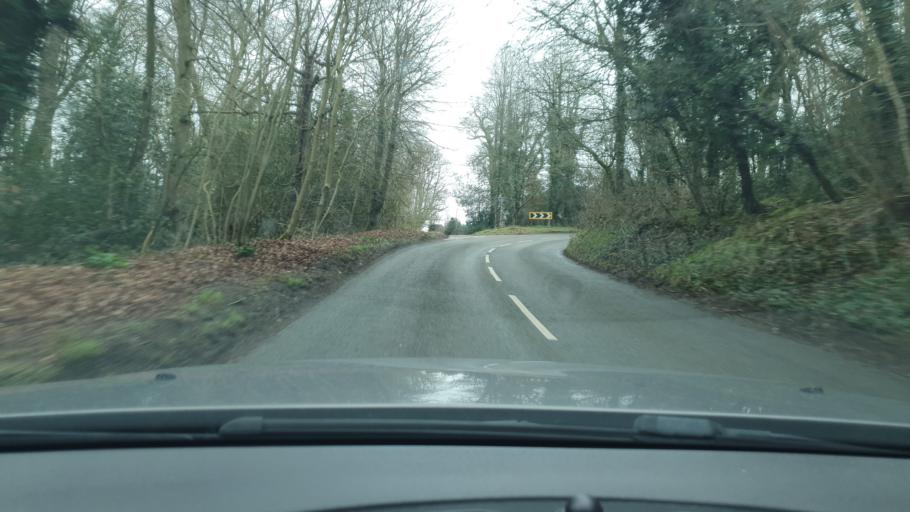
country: GB
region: England
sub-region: Oxfordshire
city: Rotherfield Peppard
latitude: 51.5407
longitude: -0.9561
